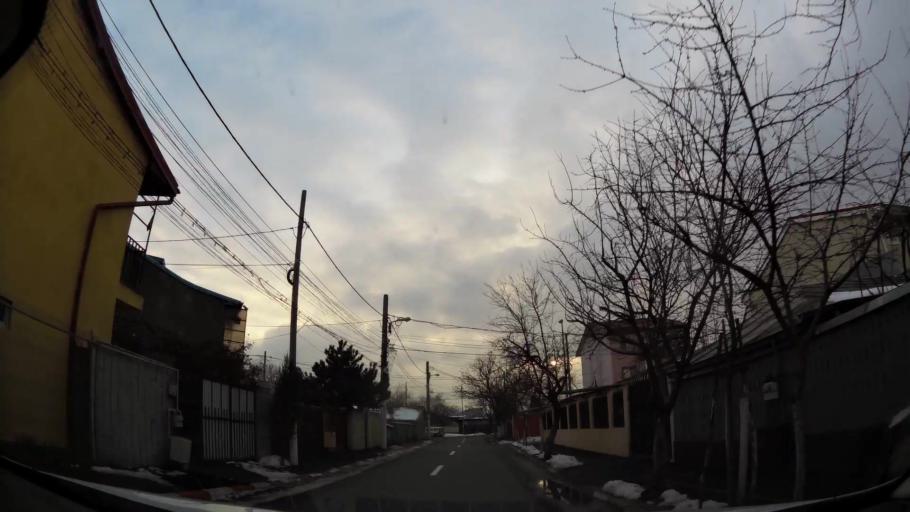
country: RO
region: Ilfov
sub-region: Voluntari City
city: Voluntari
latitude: 44.4816
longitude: 26.1810
